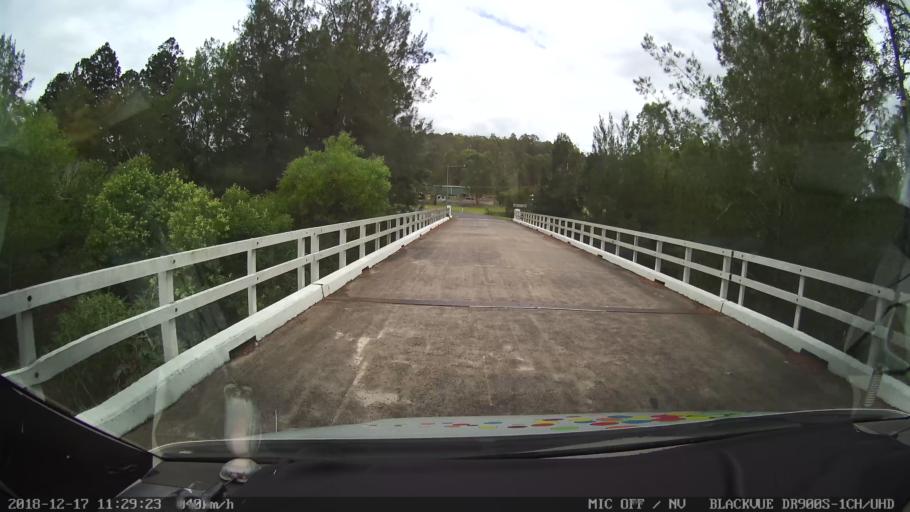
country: AU
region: New South Wales
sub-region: Kyogle
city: Kyogle
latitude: -28.7395
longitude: 152.6291
